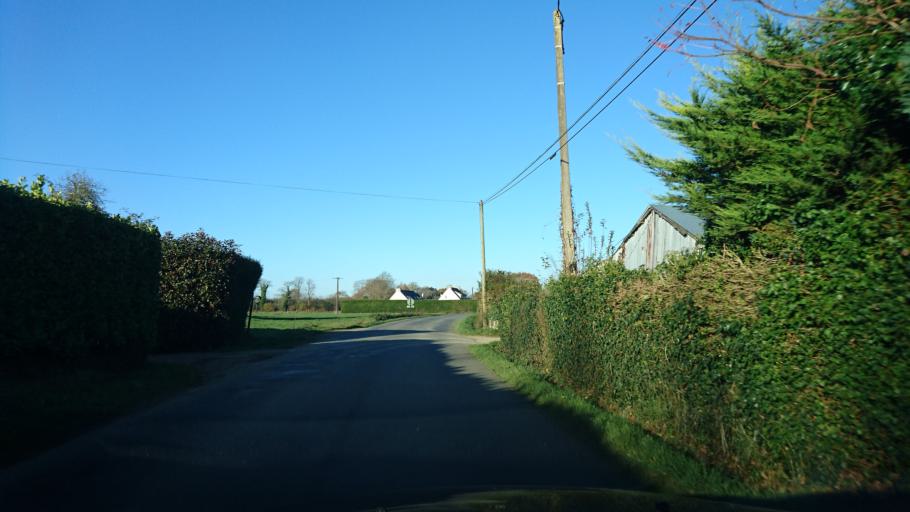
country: FR
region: Brittany
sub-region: Departement des Cotes-d'Armor
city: Pedernec
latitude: 48.5853
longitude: -3.2623
